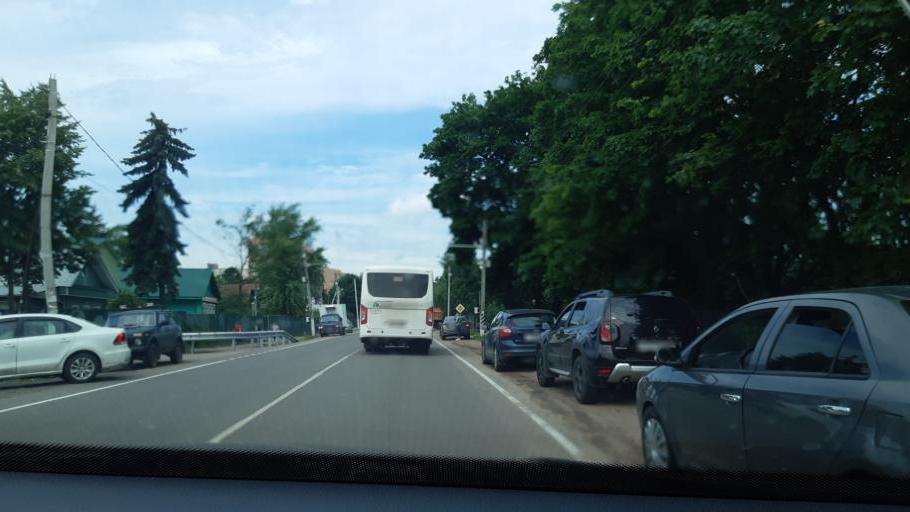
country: RU
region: Moskovskaya
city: Golitsyno
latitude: 55.6170
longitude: 36.9864
